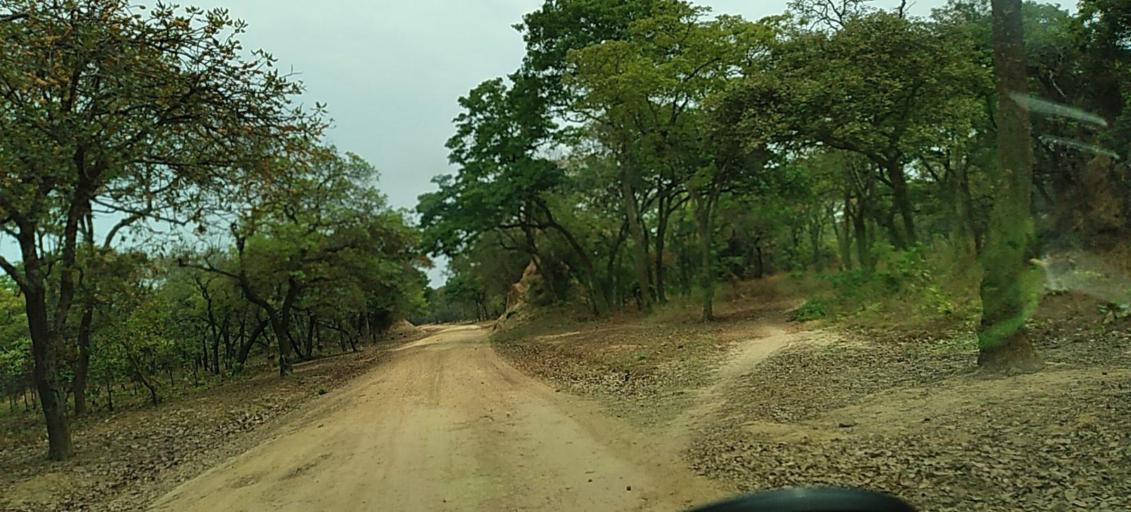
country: ZM
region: North-Western
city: Solwezi
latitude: -12.9327
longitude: 26.5597
